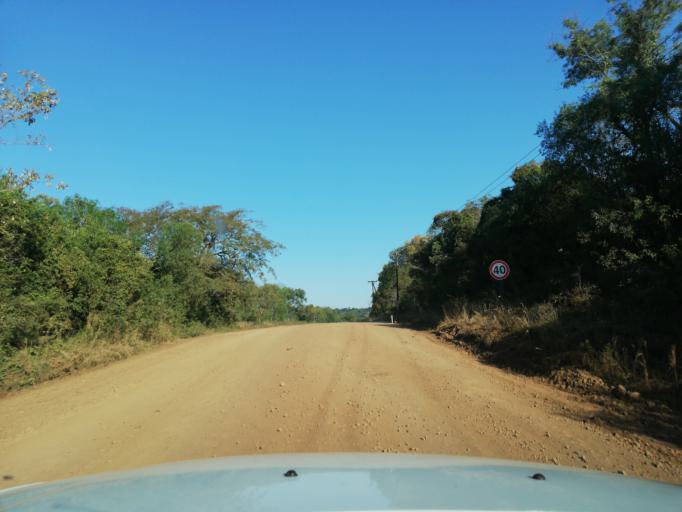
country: AR
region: Misiones
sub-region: Departamento de Candelaria
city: Candelaria
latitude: -27.5544
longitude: -55.7074
